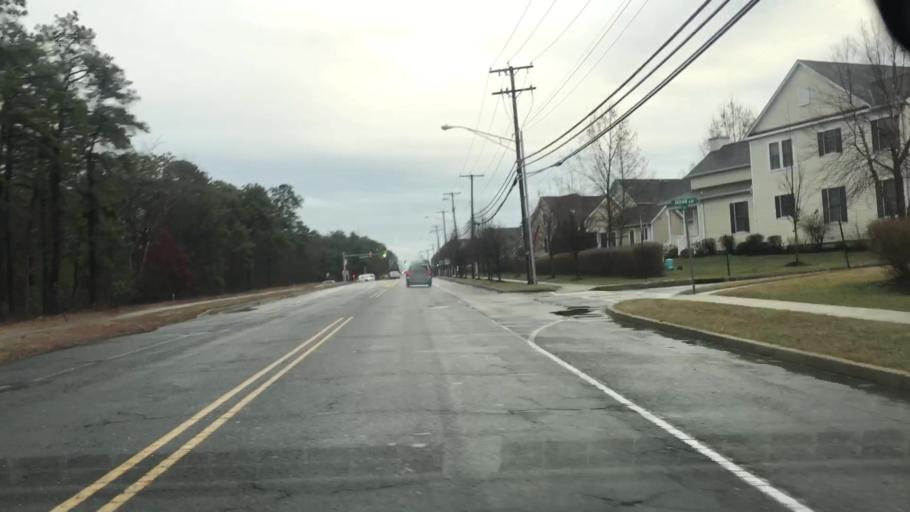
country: US
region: New Jersey
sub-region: Ocean County
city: Lakewood
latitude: 40.0743
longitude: -74.2035
